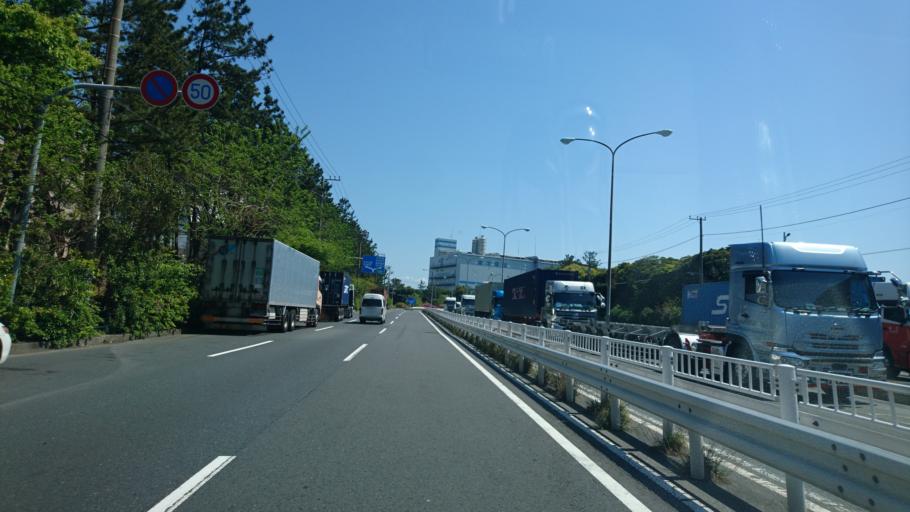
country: JP
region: Kanagawa
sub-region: Kawasaki-shi
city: Kawasaki
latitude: 35.5899
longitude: 139.7692
